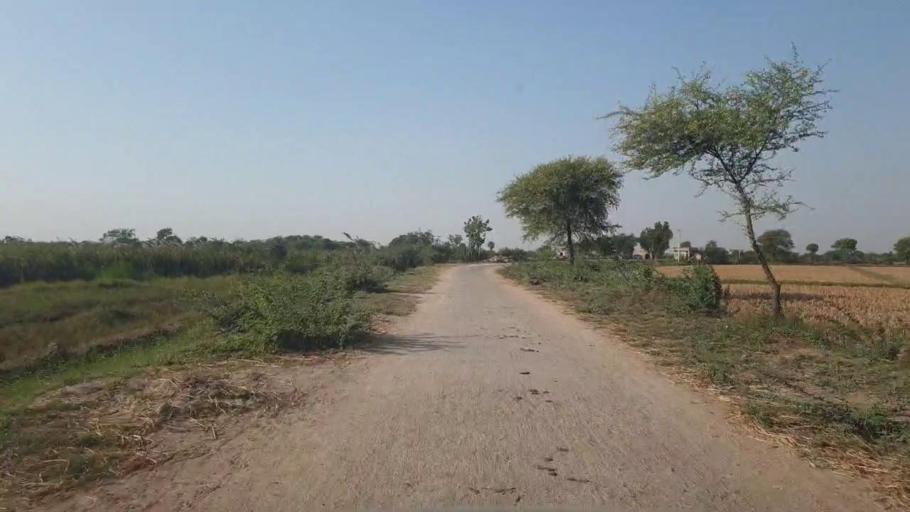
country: PK
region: Sindh
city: Badin
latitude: 24.6553
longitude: 68.8117
